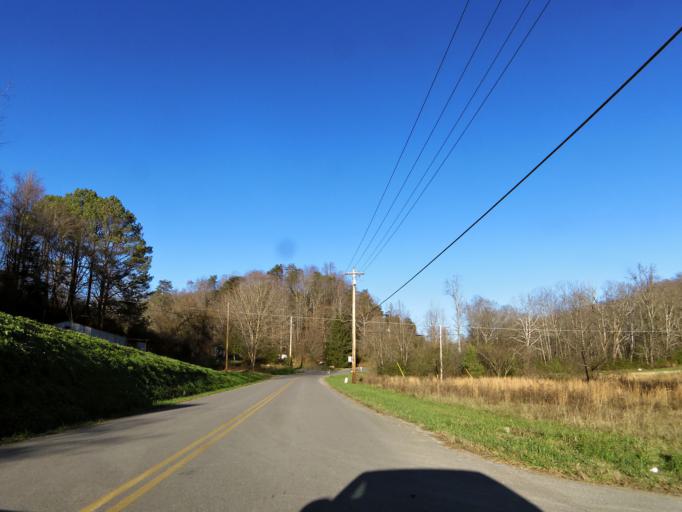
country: US
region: Tennessee
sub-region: Anderson County
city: Oak Ridge
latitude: 36.0890
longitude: -84.2362
